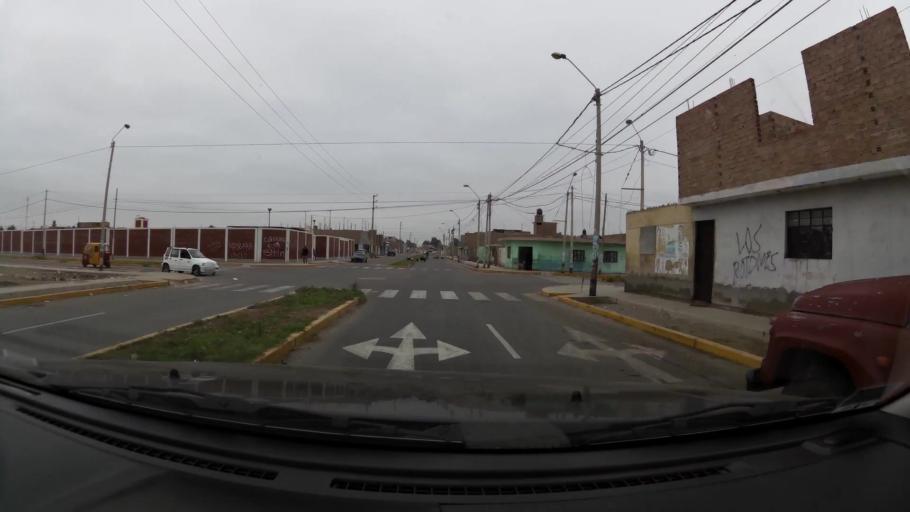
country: PE
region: Ica
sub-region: Provincia de Pisco
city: Pisco
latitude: -13.7199
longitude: -76.2043
